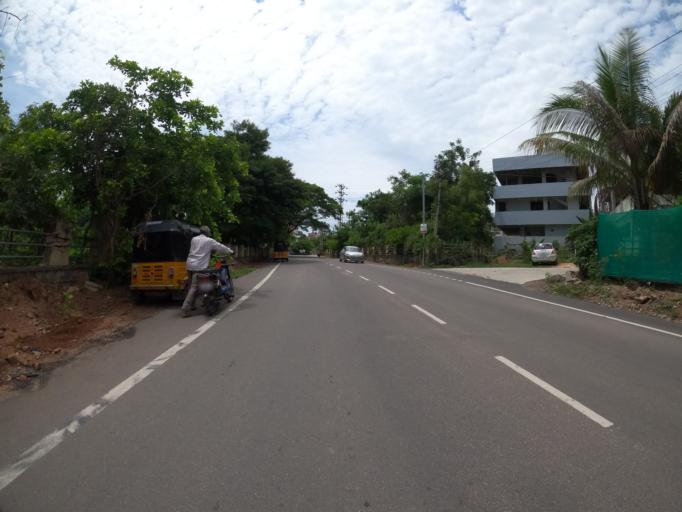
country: IN
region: Telangana
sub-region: Hyderabad
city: Hyderabad
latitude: 17.3663
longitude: 78.4152
